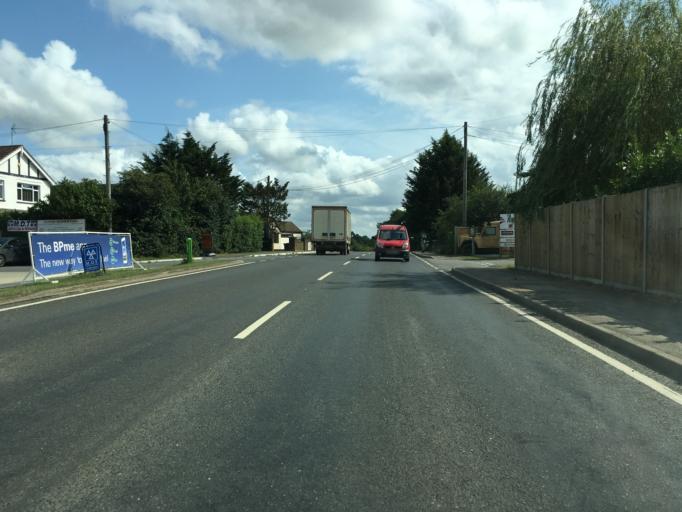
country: GB
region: England
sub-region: Kent
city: Headcorn
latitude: 51.2009
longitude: 0.5944
